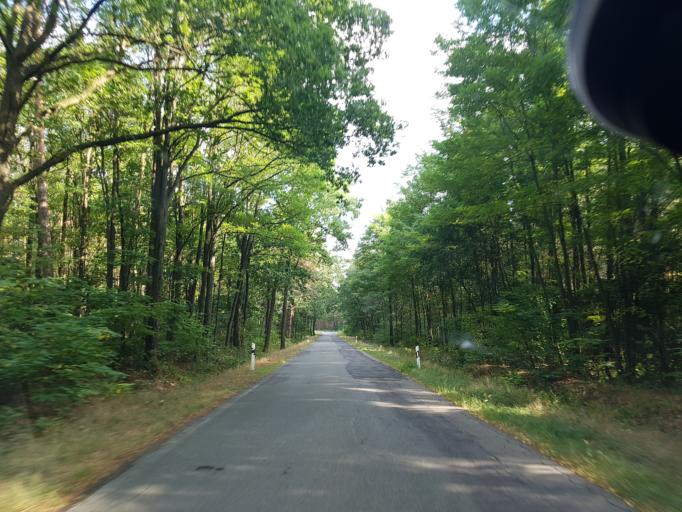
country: DE
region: Brandenburg
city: Bronkow
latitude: 51.6883
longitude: 13.8878
